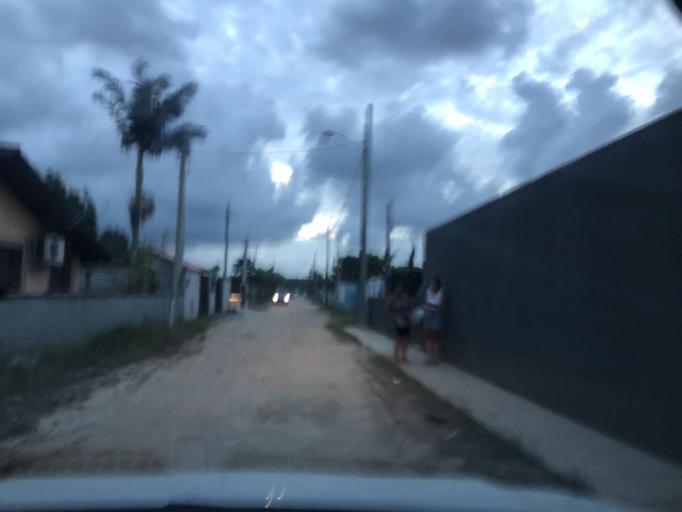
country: BR
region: Santa Catarina
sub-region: Sao Francisco Do Sul
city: Sao Francisco do Sul
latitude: -26.2247
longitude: -48.5234
